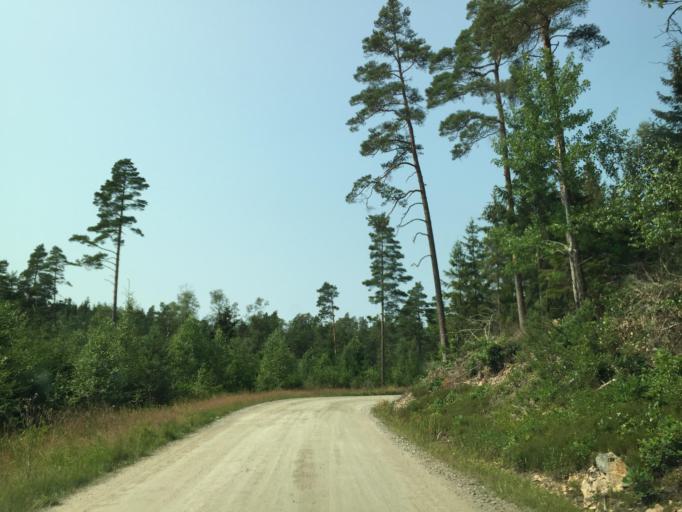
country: SE
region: Vaestra Goetaland
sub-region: Lilla Edets Kommun
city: Lilla Edet
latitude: 58.2325
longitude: 12.1120
